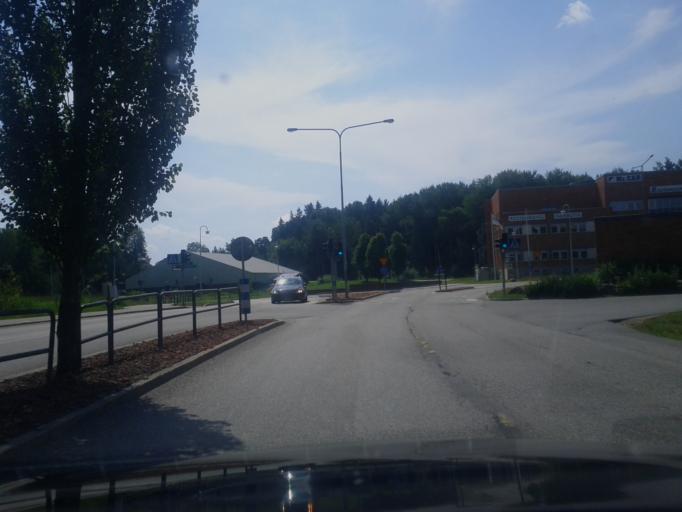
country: SE
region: Stockholm
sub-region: Taby Kommun
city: Taby
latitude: 59.4460
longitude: 18.1221
